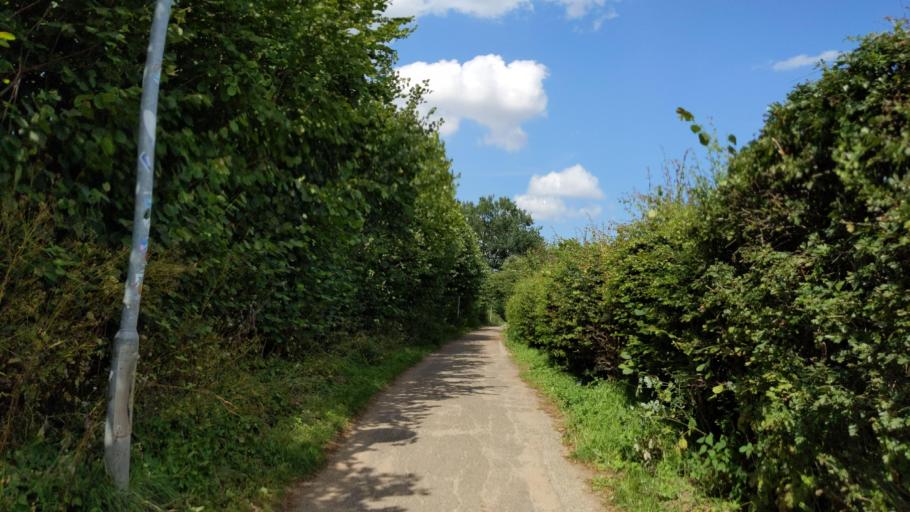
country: DE
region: Mecklenburg-Vorpommern
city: Selmsdorf
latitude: 53.9077
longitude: 10.8123
